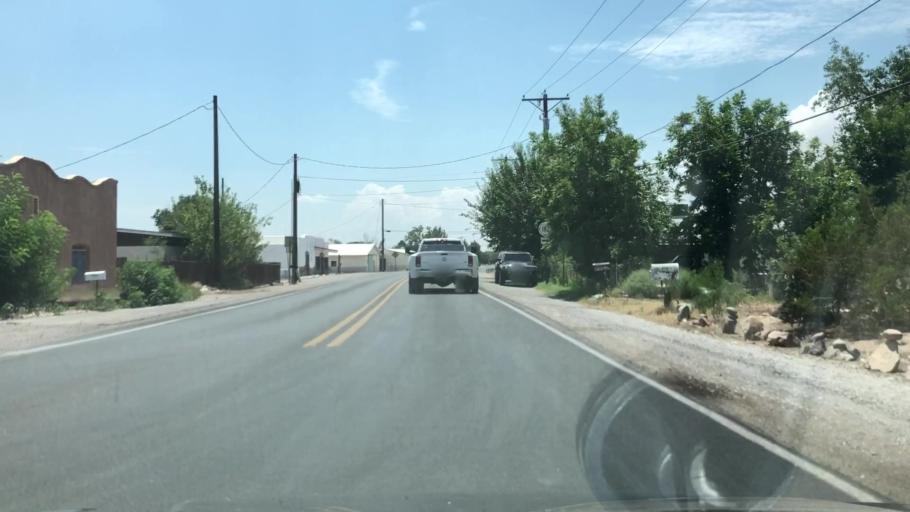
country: US
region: New Mexico
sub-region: Dona Ana County
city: La Union
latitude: 31.9560
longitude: -106.6454
